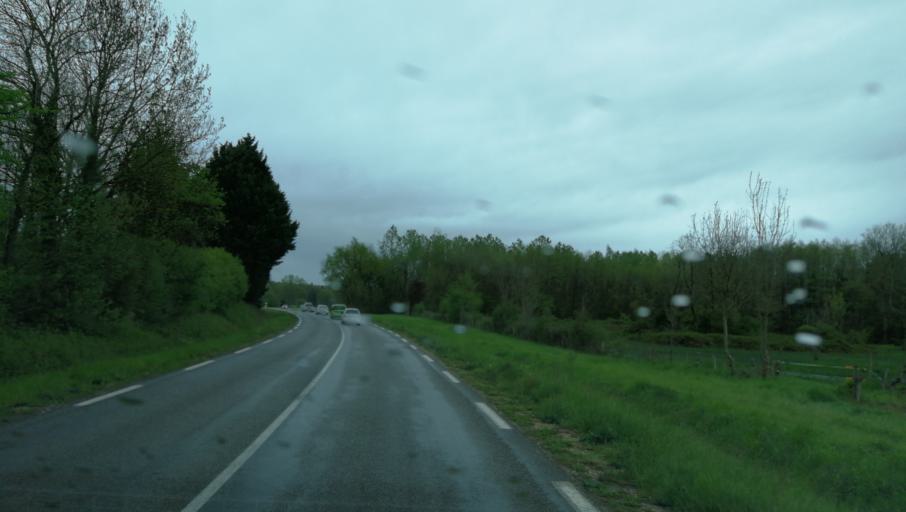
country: FR
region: Franche-Comte
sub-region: Departement du Jura
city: Bletterans
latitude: 46.7151
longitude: 5.4753
